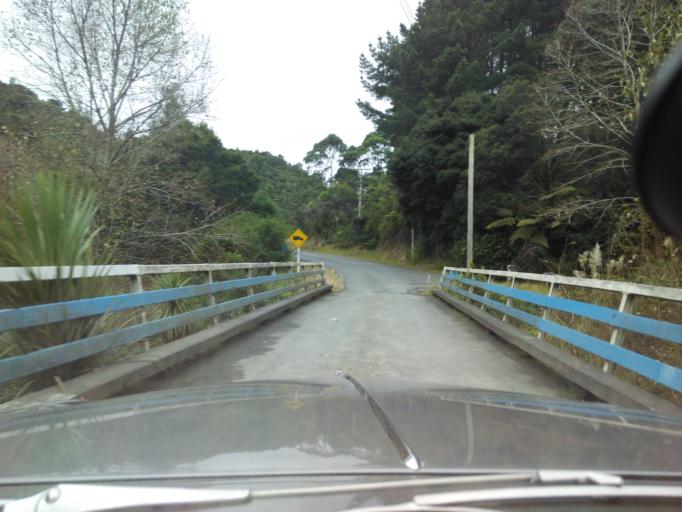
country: NZ
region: Auckland
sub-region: Auckland
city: Warkworth
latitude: -36.5396
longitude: 174.5755
